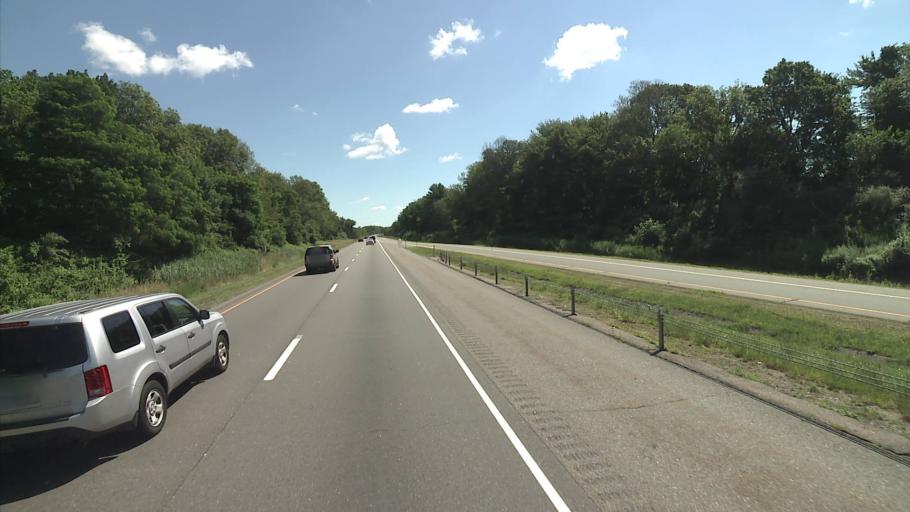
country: US
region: Connecticut
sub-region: New London County
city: Old Mystic
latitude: 41.3797
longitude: -71.9021
